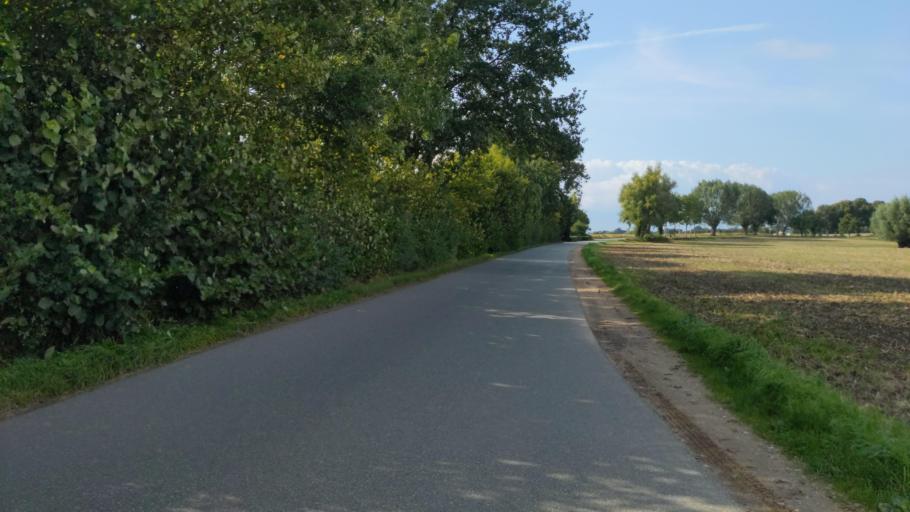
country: DE
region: Mecklenburg-Vorpommern
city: Kalkhorst
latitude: 53.9773
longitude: 11.0081
